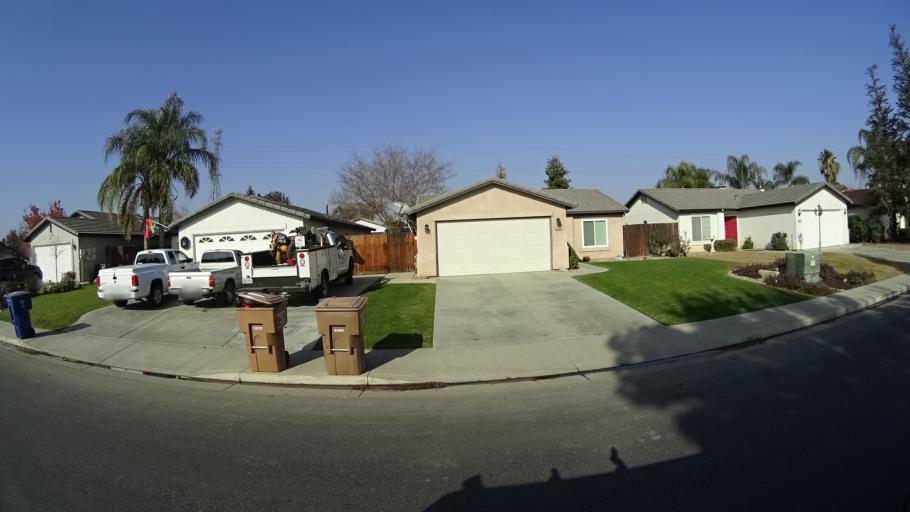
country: US
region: California
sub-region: Kern County
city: Greenacres
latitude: 35.3962
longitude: -119.0722
